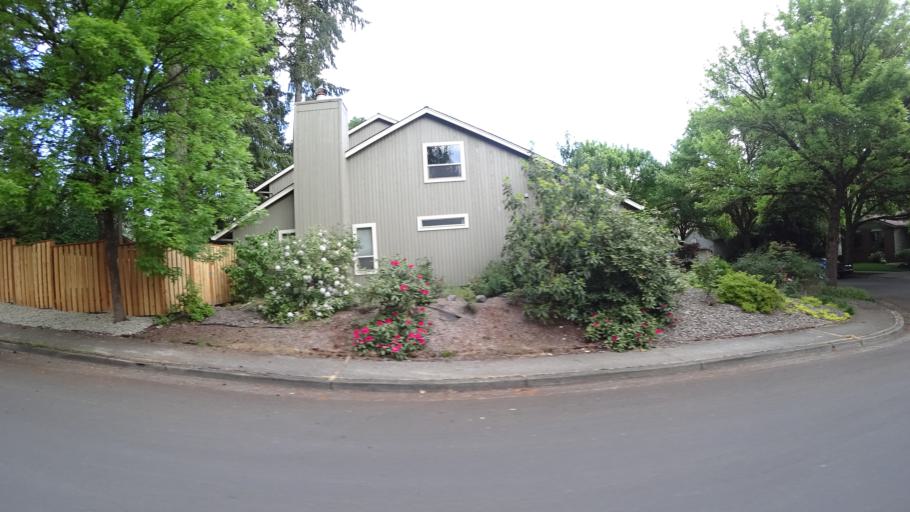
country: US
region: Oregon
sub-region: Washington County
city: Beaverton
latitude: 45.4738
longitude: -122.8367
